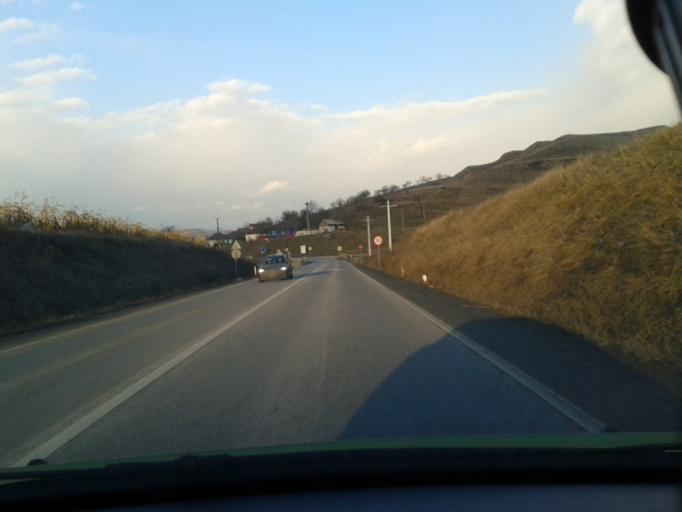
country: RO
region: Sibiu
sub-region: Comuna Tarnava
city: Tarnava
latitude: 46.1285
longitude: 24.2975
